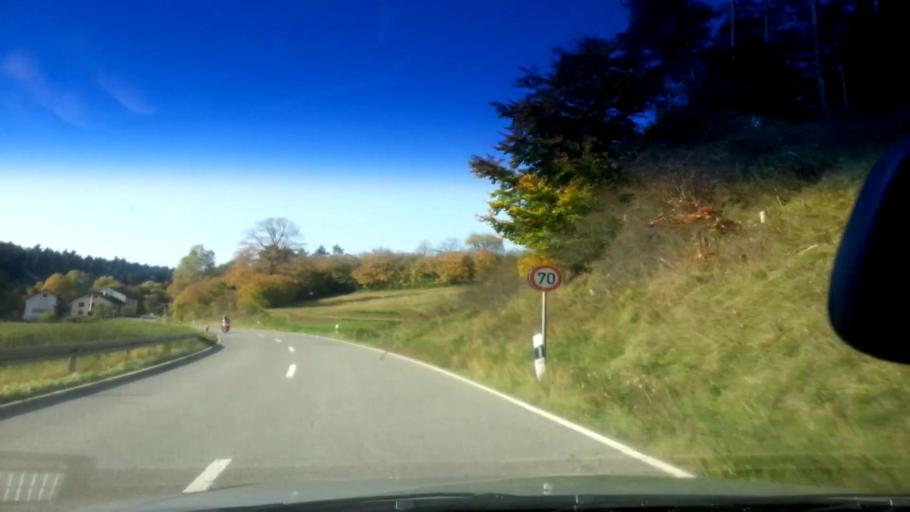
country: DE
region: Bavaria
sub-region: Upper Franconia
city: Stadelhofen
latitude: 49.9757
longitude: 11.1847
